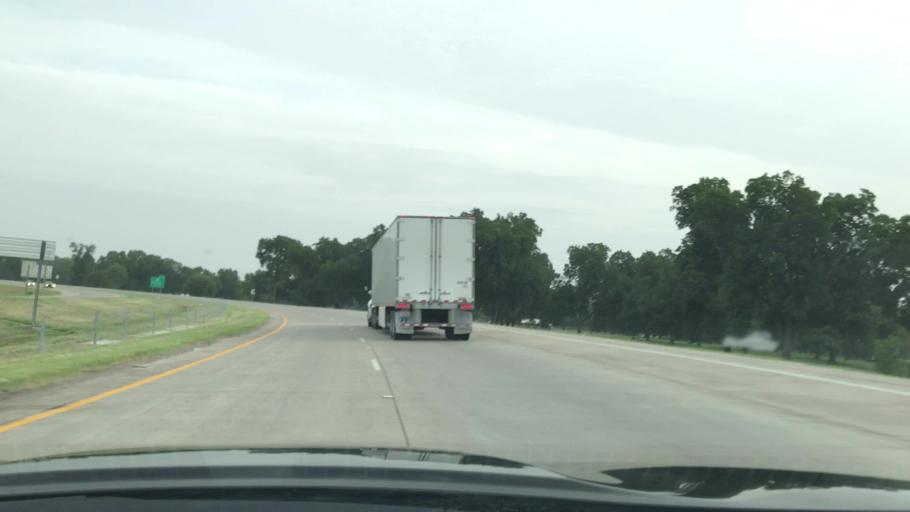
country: US
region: Louisiana
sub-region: Bossier Parish
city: Bossier City
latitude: 32.4055
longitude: -93.7145
